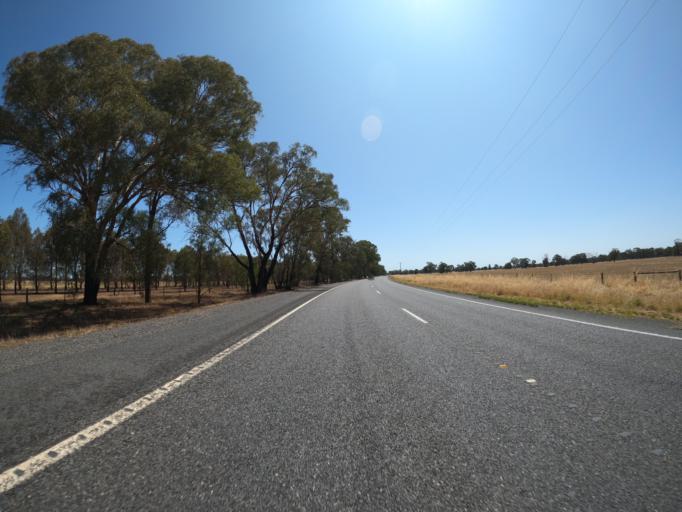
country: AU
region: New South Wales
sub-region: Corowa Shire
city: Corowa
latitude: -36.0671
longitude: 146.3902
